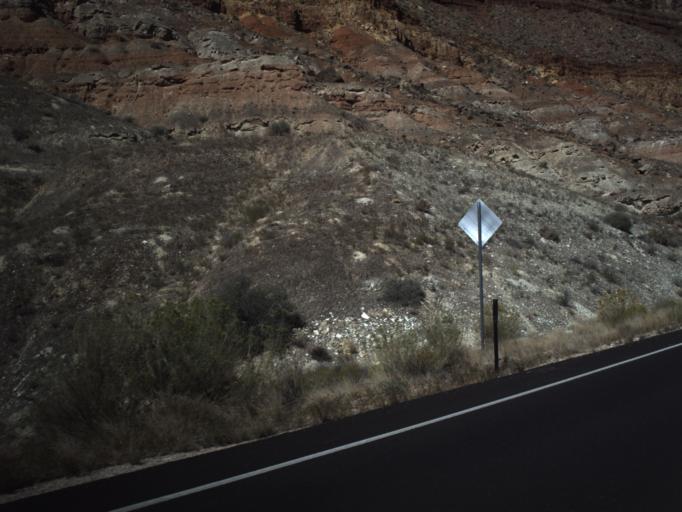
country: US
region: Utah
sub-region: Washington County
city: Hurricane
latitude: 37.1810
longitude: -113.3966
